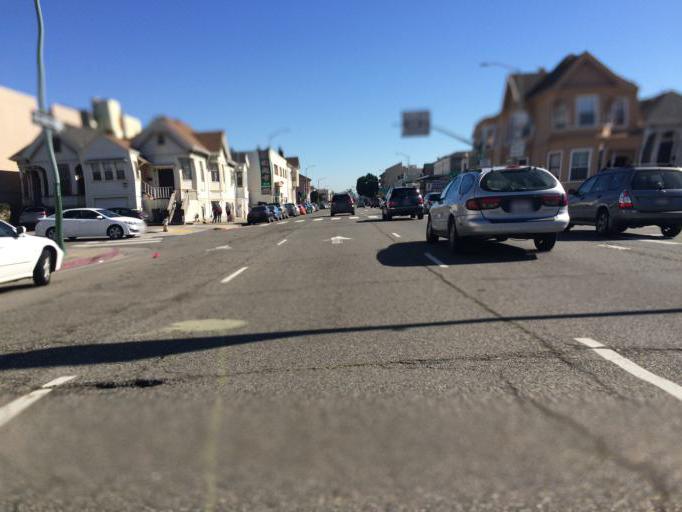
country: US
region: California
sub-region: Alameda County
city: Oakland
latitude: 37.7978
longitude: -122.2697
